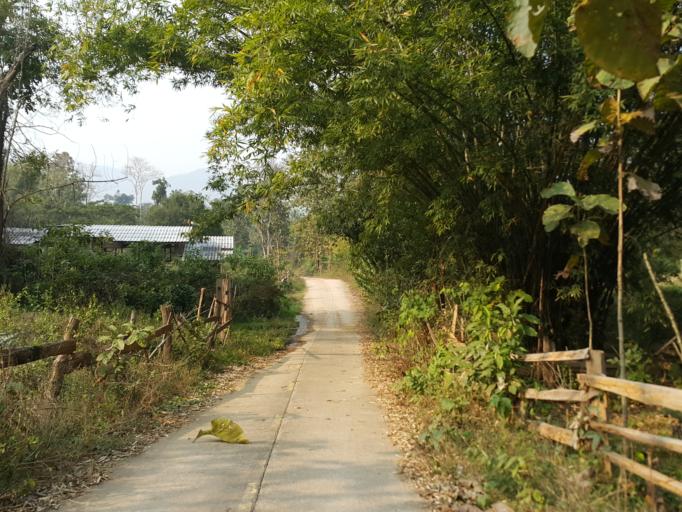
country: TH
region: Lamphun
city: Li
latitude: 17.6042
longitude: 98.9639
